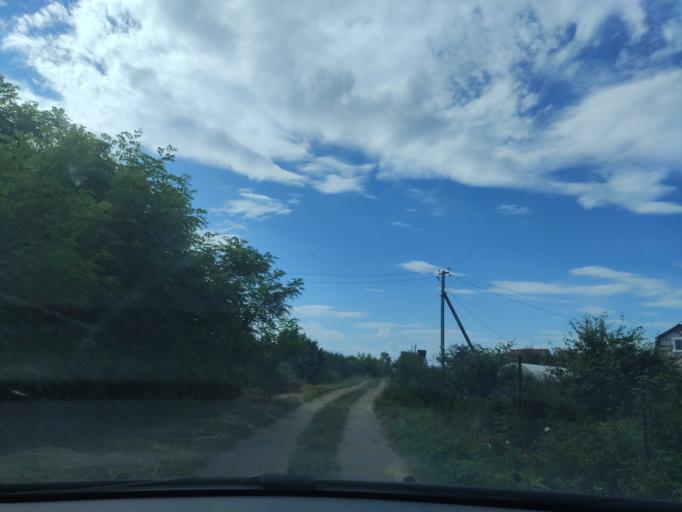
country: RU
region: Ulyanovsk
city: Cherdakly
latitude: 54.4421
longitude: 48.8972
